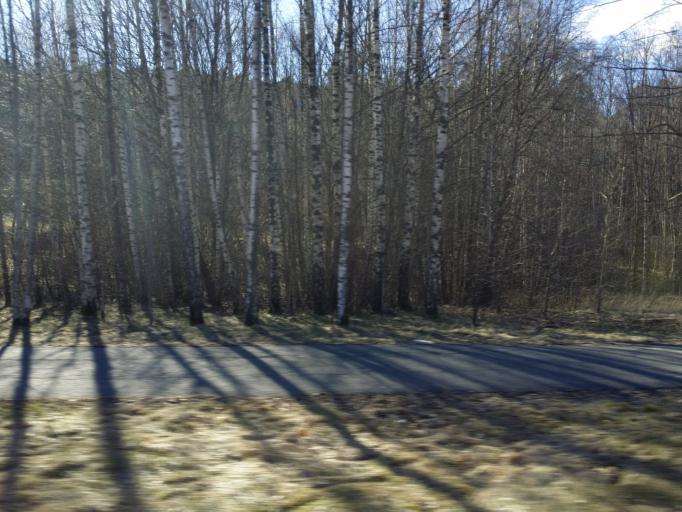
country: NO
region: Akershus
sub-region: Oppegard
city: Kolbotn
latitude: 59.8409
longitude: 10.7778
